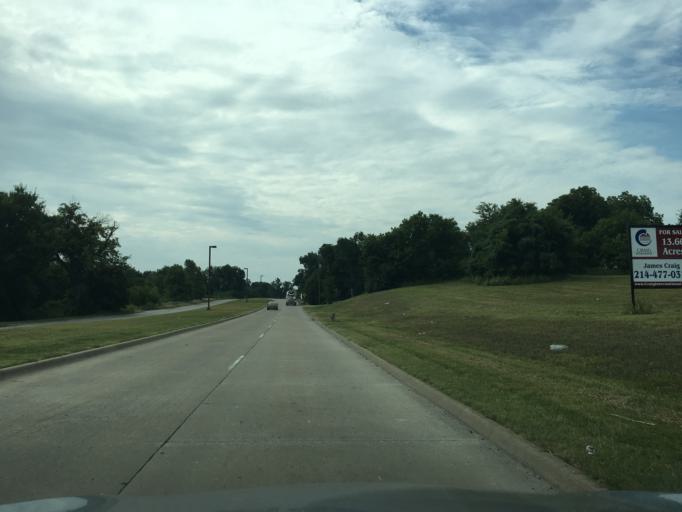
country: US
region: Texas
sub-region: Collin County
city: McKinney
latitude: 33.1973
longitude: -96.5986
